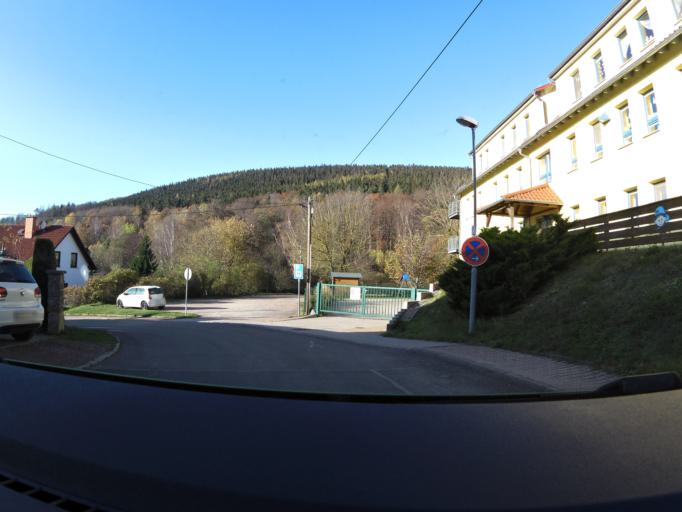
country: DE
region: Thuringia
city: Ruhla
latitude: 50.8868
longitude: 10.3888
